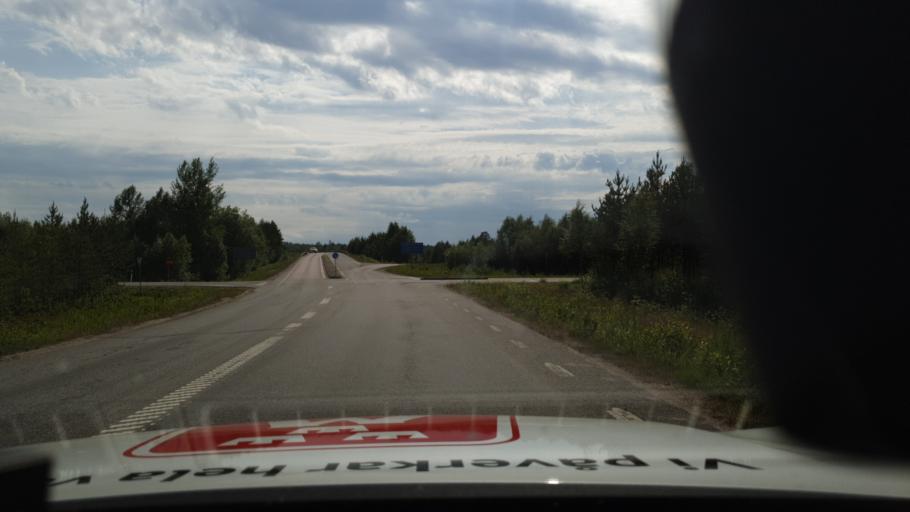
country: SE
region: Norrbotten
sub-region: Lulea Kommun
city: Ranea
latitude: 65.8431
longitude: 22.2621
